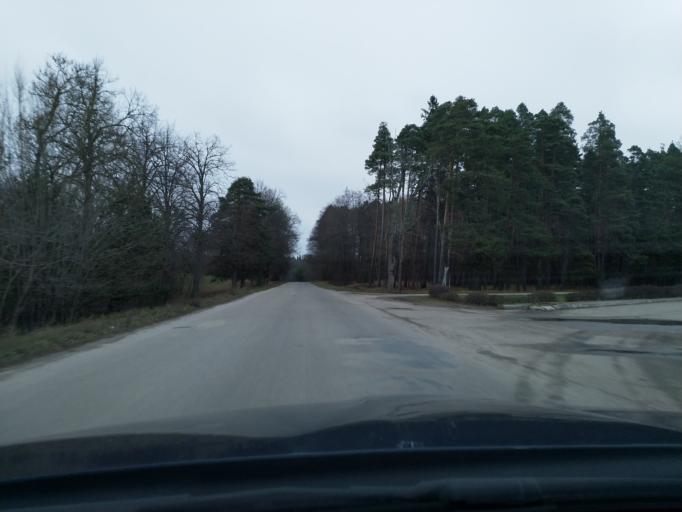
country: LV
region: Ventspils Rajons
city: Piltene
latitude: 57.1200
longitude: 21.8113
